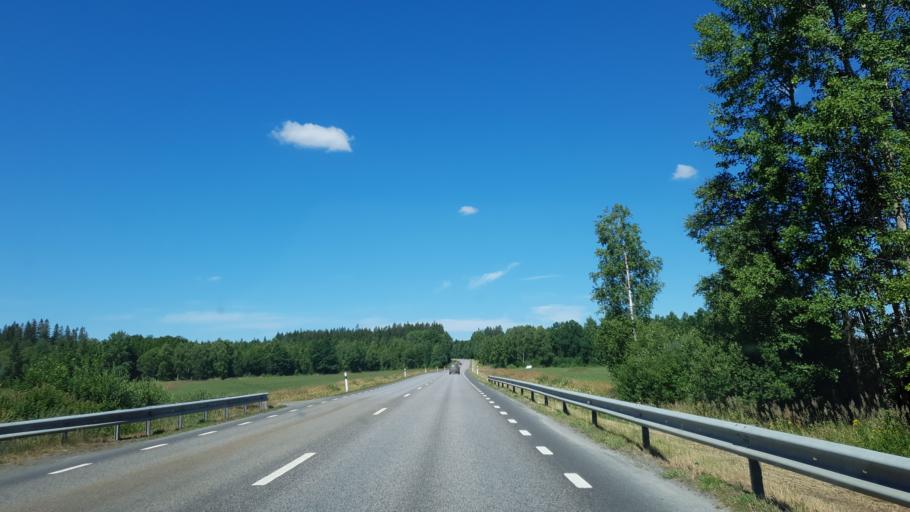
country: SE
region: Joenkoeping
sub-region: Varnamo Kommun
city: Bor
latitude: 57.1345
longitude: 14.1189
